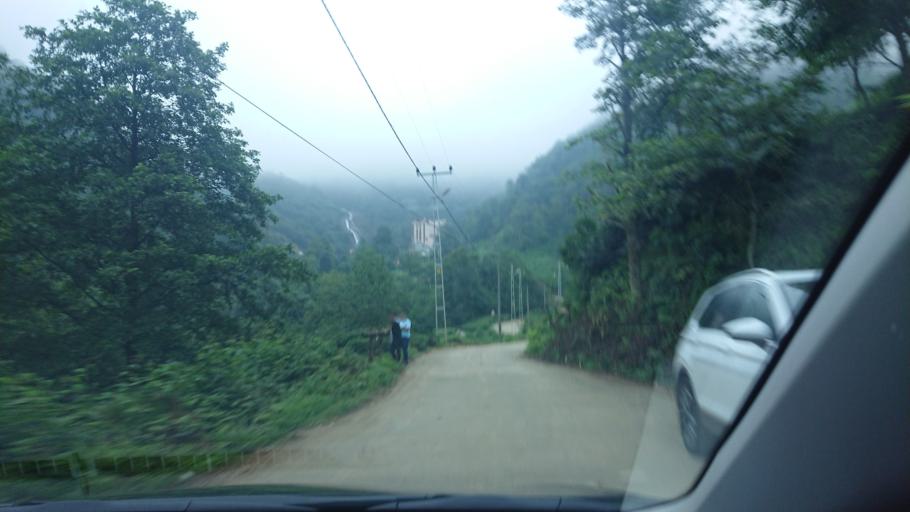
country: TR
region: Rize
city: Kaptanpasa
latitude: 41.0458
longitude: 40.8033
